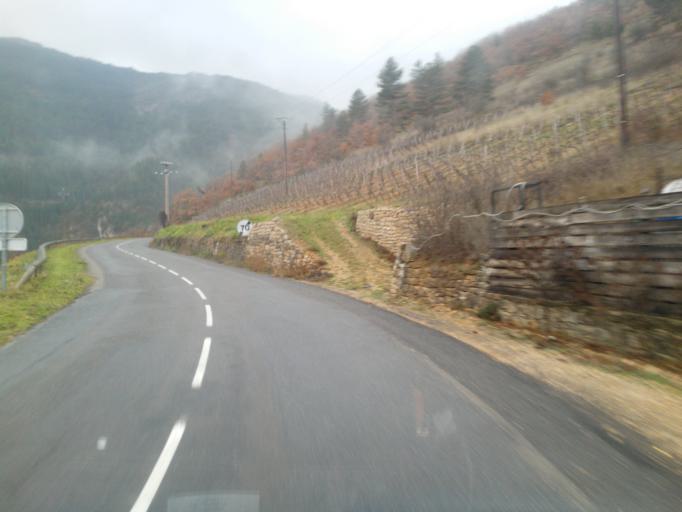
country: FR
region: Languedoc-Roussillon
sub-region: Departement de la Lozere
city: Florac
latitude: 44.3412
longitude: 3.4718
